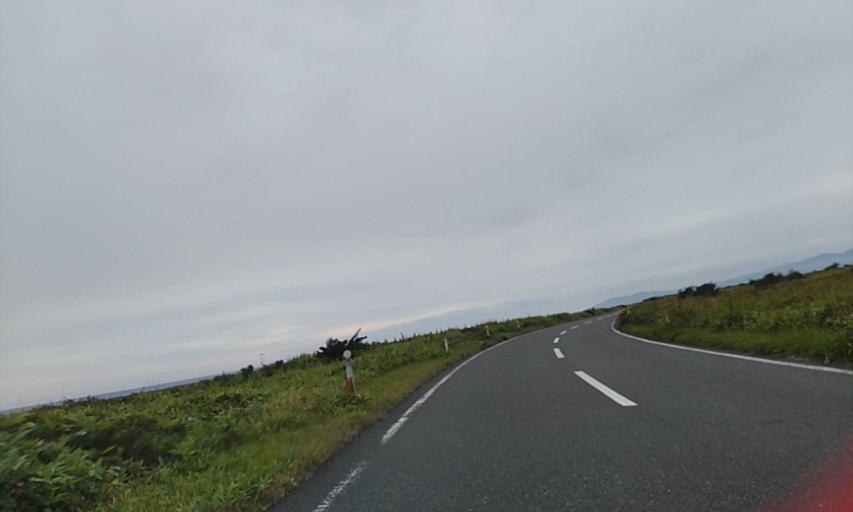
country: JP
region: Hokkaido
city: Makubetsu
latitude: 45.2503
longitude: 142.2561
